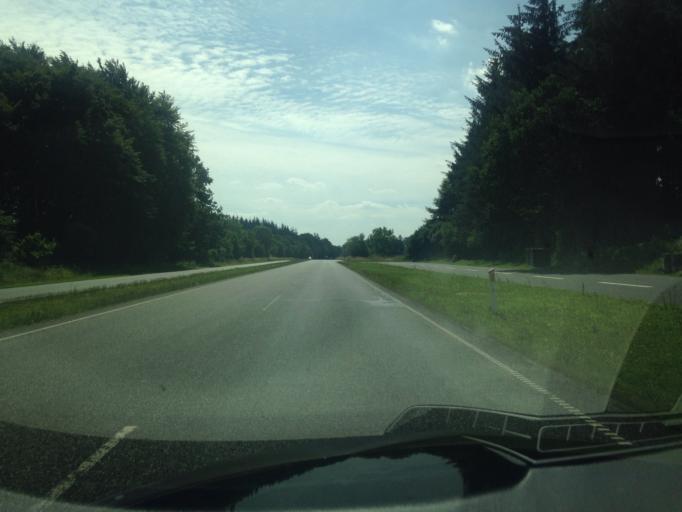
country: DK
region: South Denmark
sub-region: Kolding Kommune
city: Kolding
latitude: 55.5214
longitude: 9.4990
